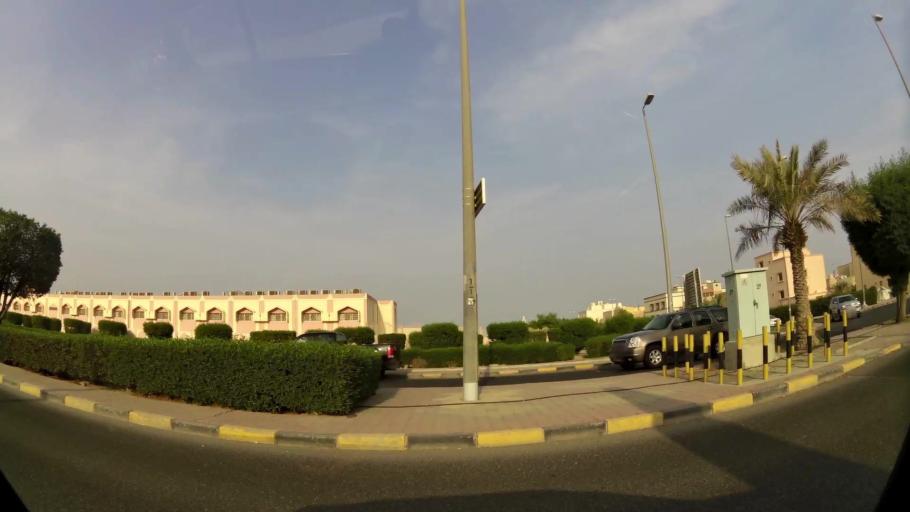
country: KW
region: Mubarak al Kabir
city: Mubarak al Kabir
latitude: 29.2127
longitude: 48.0664
